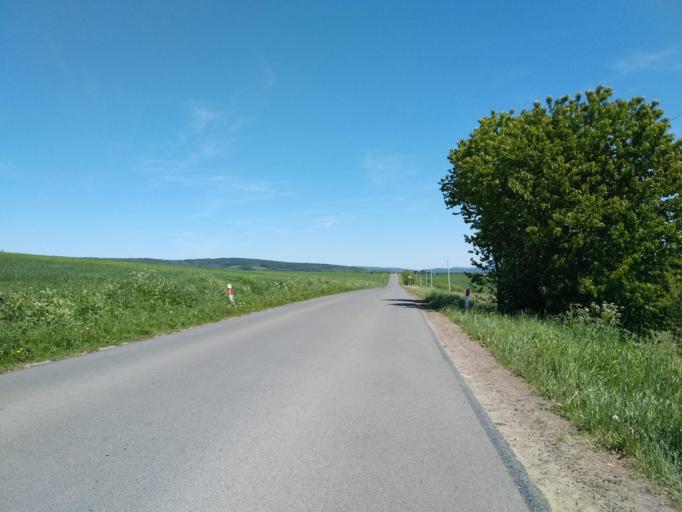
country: PL
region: Subcarpathian Voivodeship
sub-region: Powiat sanocki
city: Nowosielce-Gniewosz
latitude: 49.5413
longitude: 22.0636
